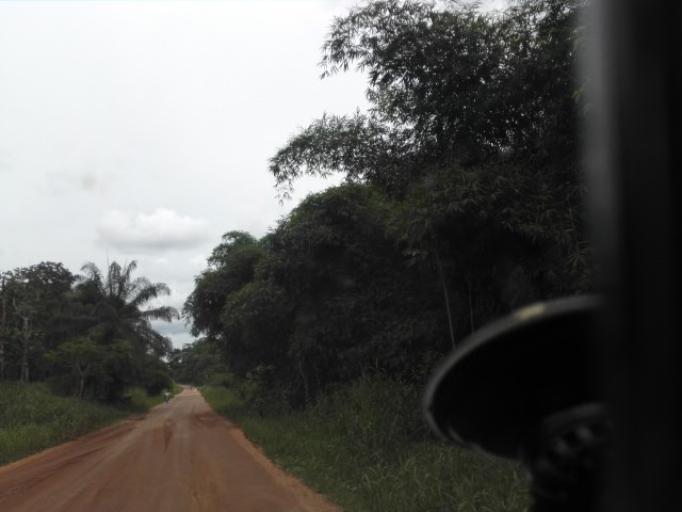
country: CD
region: Eastern Province
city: Kisangani
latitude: 0.4629
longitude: 25.3497
